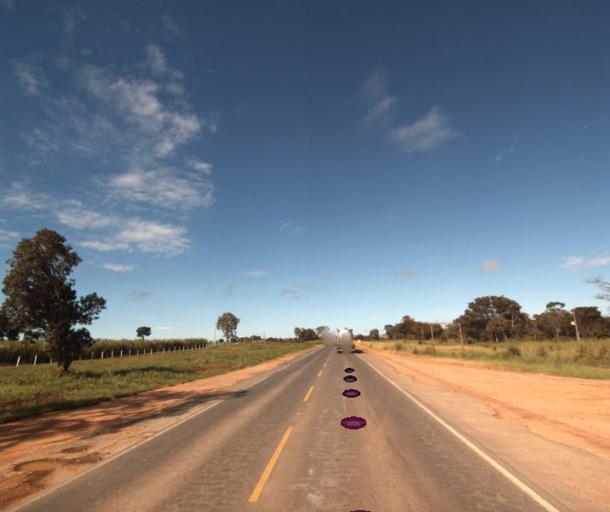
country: BR
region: Goias
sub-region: Itapaci
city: Itapaci
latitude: -14.8355
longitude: -49.3072
